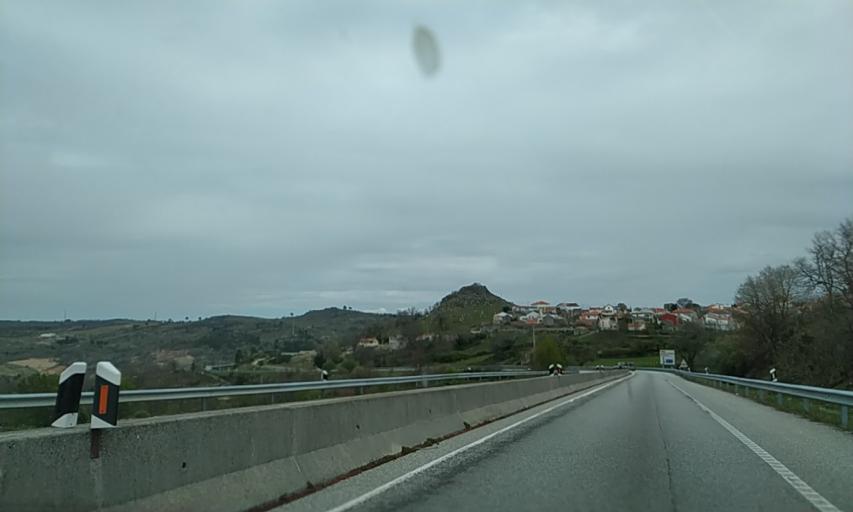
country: PT
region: Guarda
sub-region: Guarda
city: Guarda
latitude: 40.5862
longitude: -7.2673
